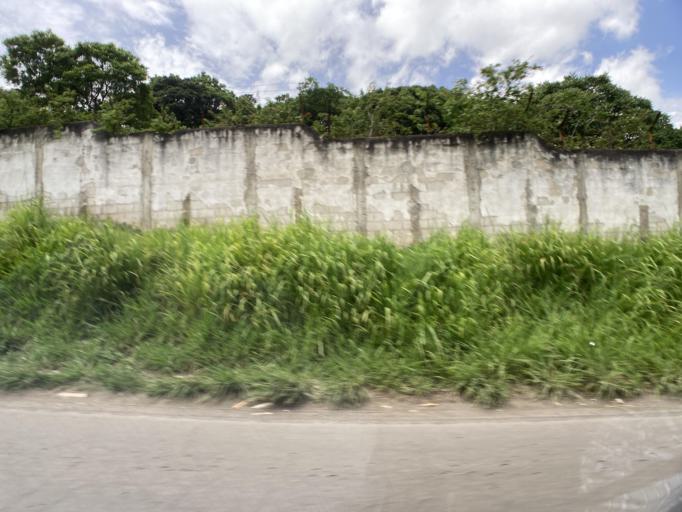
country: GT
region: Guatemala
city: Amatitlan
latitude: 14.4738
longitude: -90.5994
